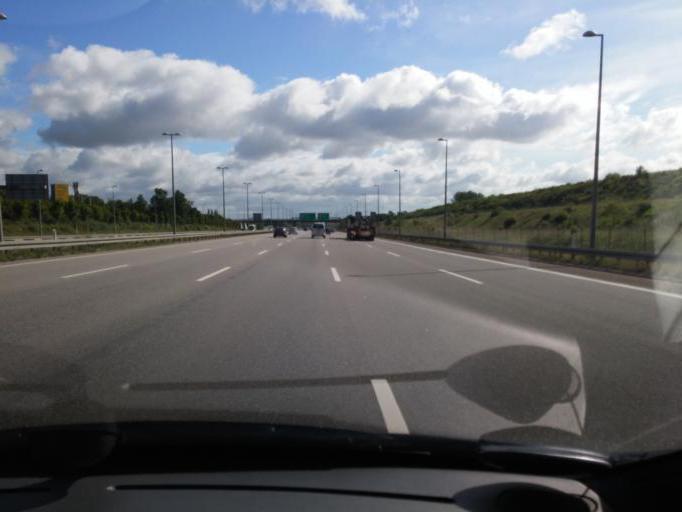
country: DK
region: Zealand
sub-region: Greve Kommune
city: Greve
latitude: 55.6067
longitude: 12.3121
